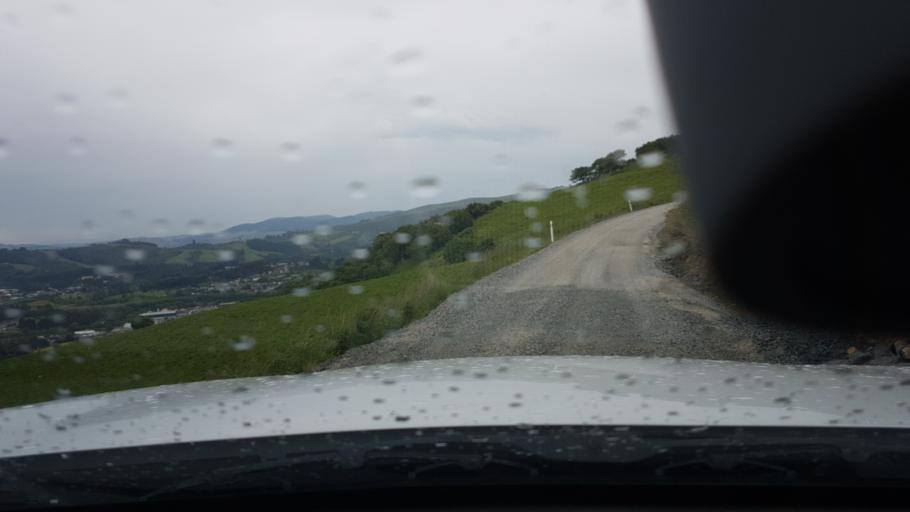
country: NZ
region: Otago
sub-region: Dunedin City
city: Dunedin
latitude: -45.9178
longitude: 170.4274
